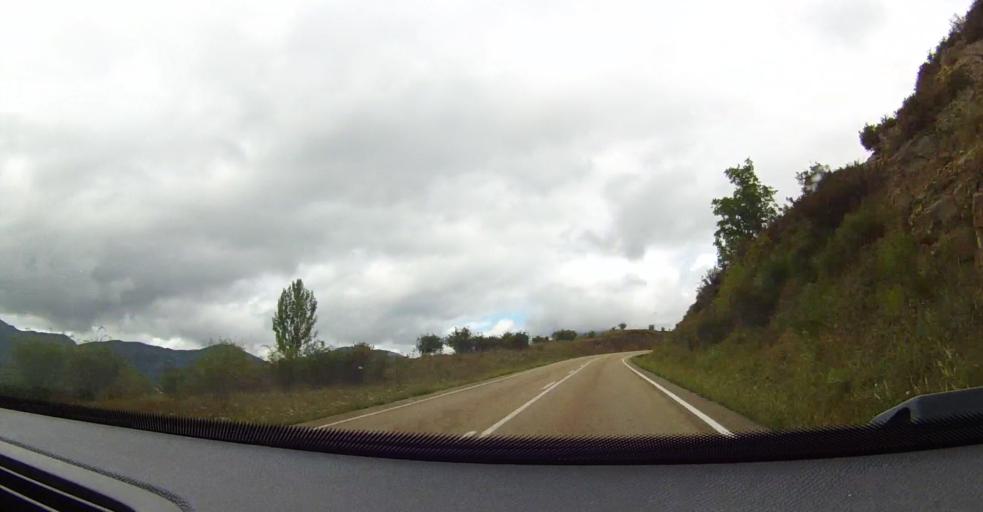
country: ES
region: Castille and Leon
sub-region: Provincia de Leon
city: Puebla de Lillo
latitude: 42.9350
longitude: -5.2724
